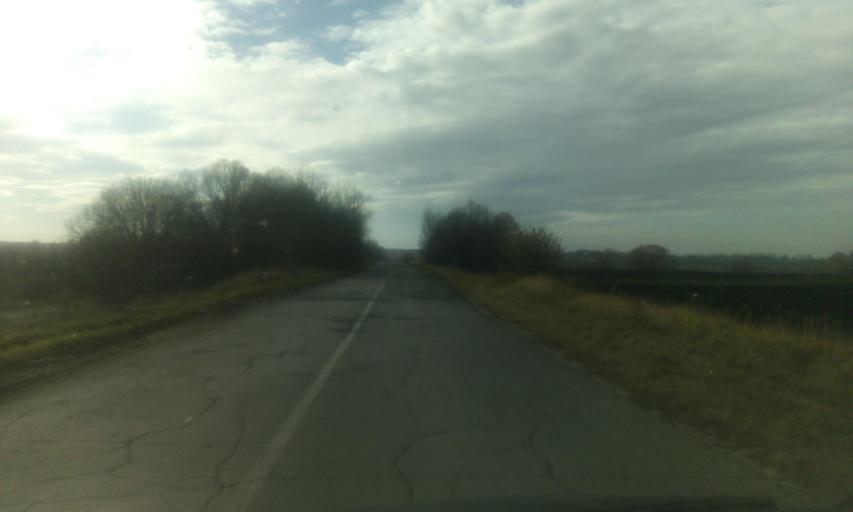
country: RU
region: Tula
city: Dubovka
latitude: 53.9549
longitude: 38.0351
